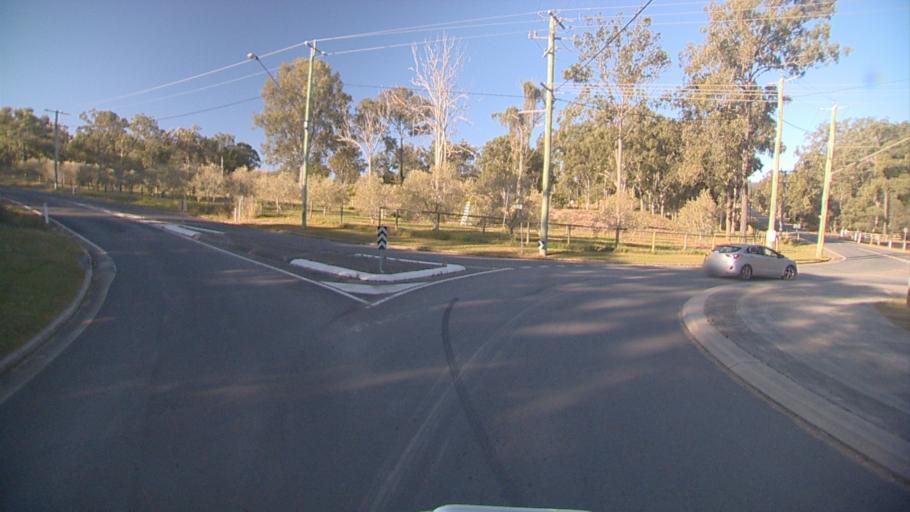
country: AU
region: Queensland
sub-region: Logan
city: Chambers Flat
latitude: -27.7702
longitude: 153.1374
